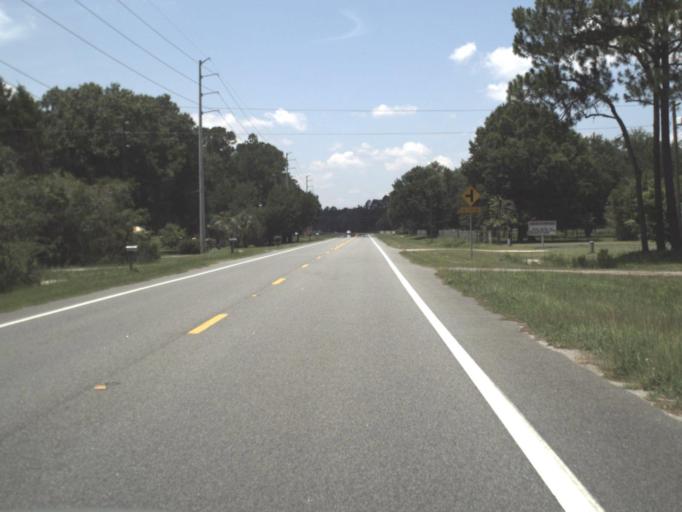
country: US
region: Florida
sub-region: Bradford County
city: Starke
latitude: 29.9544
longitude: -82.0693
